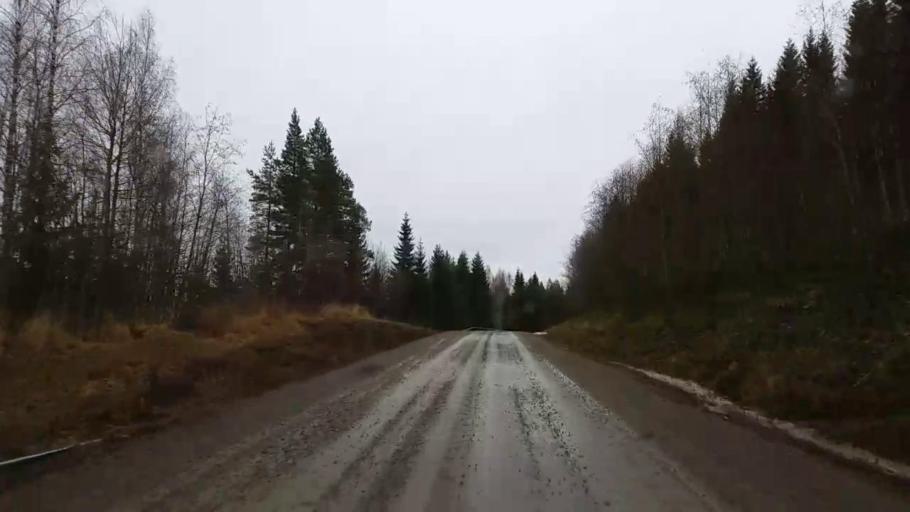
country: SE
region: Gaevleborg
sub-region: Ljusdals Kommun
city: Farila
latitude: 62.0972
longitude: 15.7555
